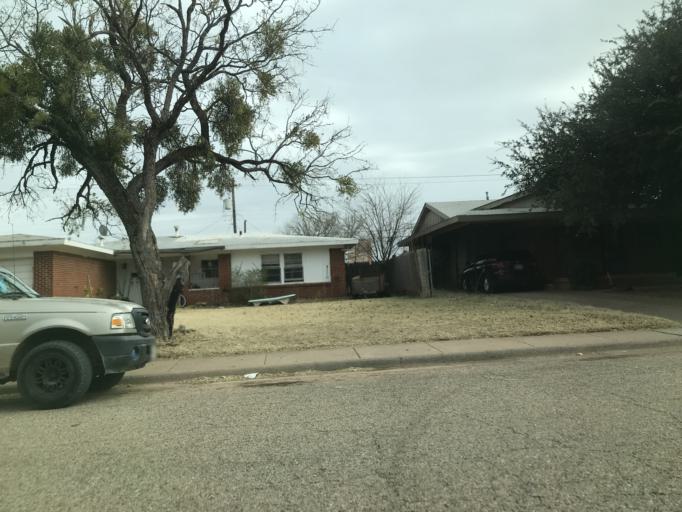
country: US
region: Texas
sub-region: Taylor County
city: Abilene
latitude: 32.4636
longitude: -99.7611
